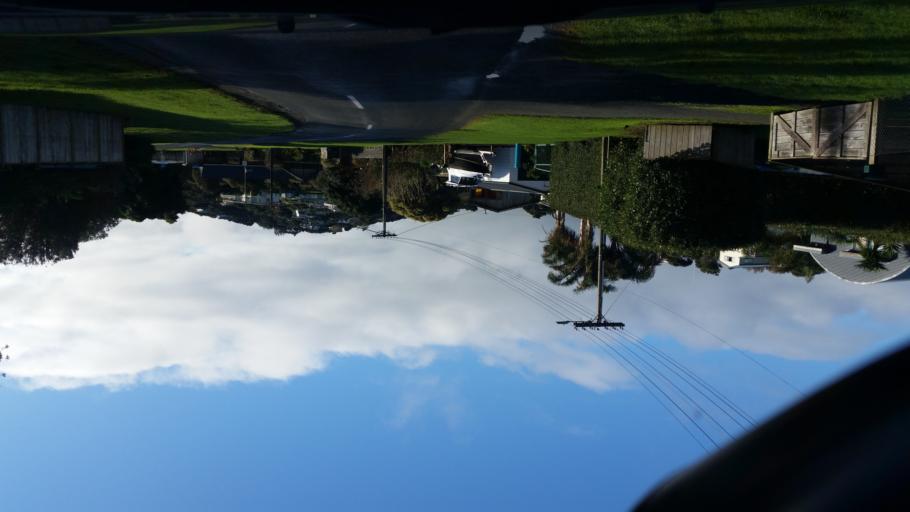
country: NZ
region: Auckland
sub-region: Auckland
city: Wellsford
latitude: -36.0887
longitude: 174.5890
